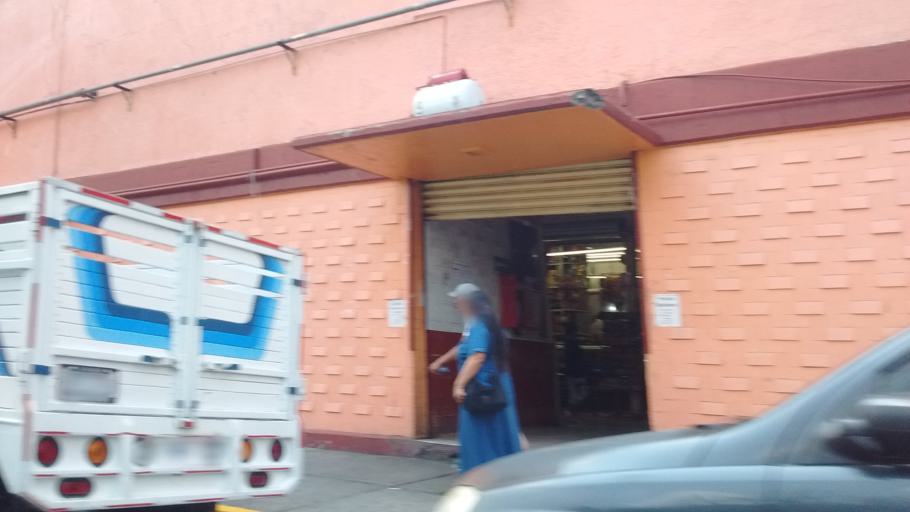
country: MX
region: Mexico City
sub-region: Iztacalco
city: Iztacalco
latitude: 19.4126
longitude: -99.0910
